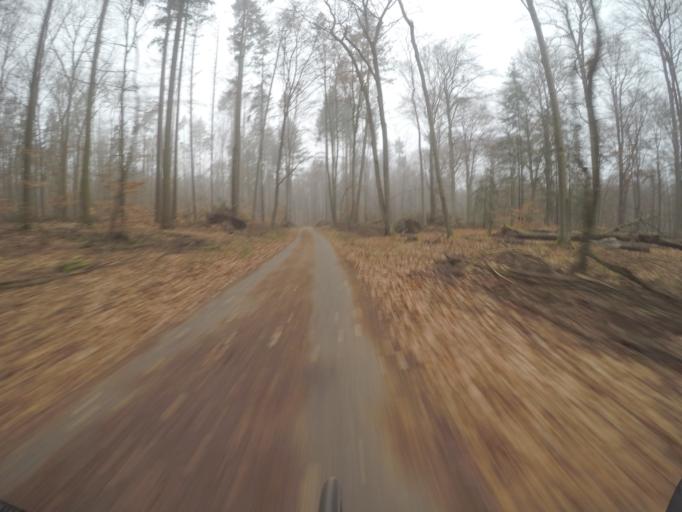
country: DE
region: Brandenburg
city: Wandlitz
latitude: 52.7415
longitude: 13.4929
